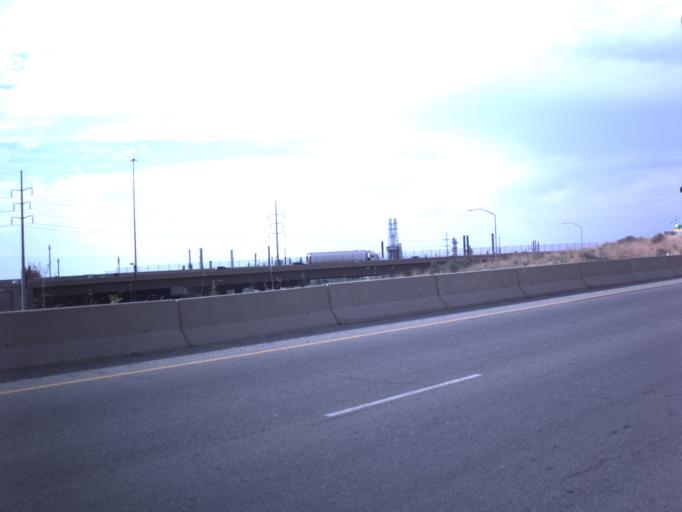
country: US
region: Utah
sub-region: Davis County
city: North Salt Lake
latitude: 40.8142
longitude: -111.9186
